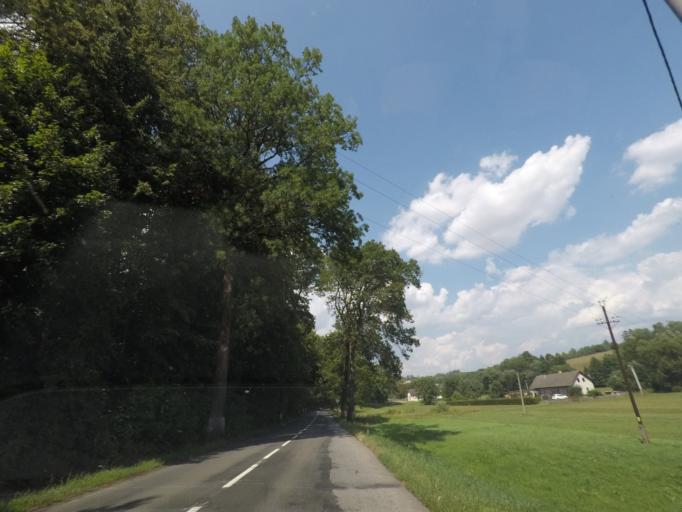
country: CZ
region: Kralovehradecky
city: Zadni Mostek
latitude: 50.5301
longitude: 15.6785
